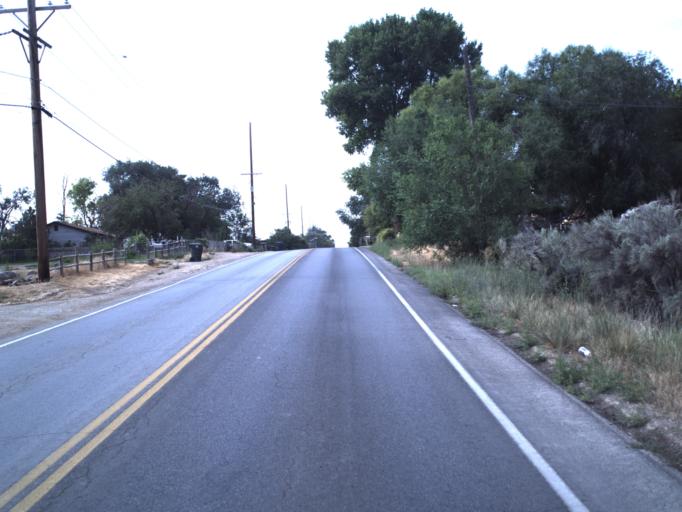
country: US
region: Utah
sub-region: Uintah County
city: Naples
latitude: 40.4083
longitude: -109.4991
